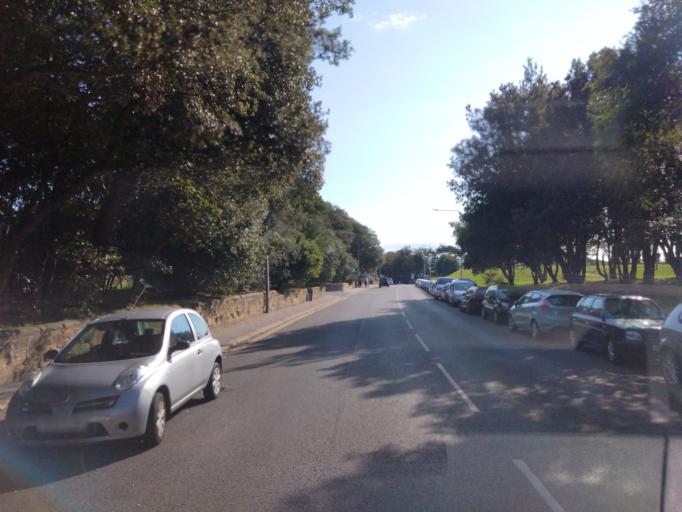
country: GB
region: England
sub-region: East Sussex
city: Hastings
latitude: 50.8574
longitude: 0.5675
